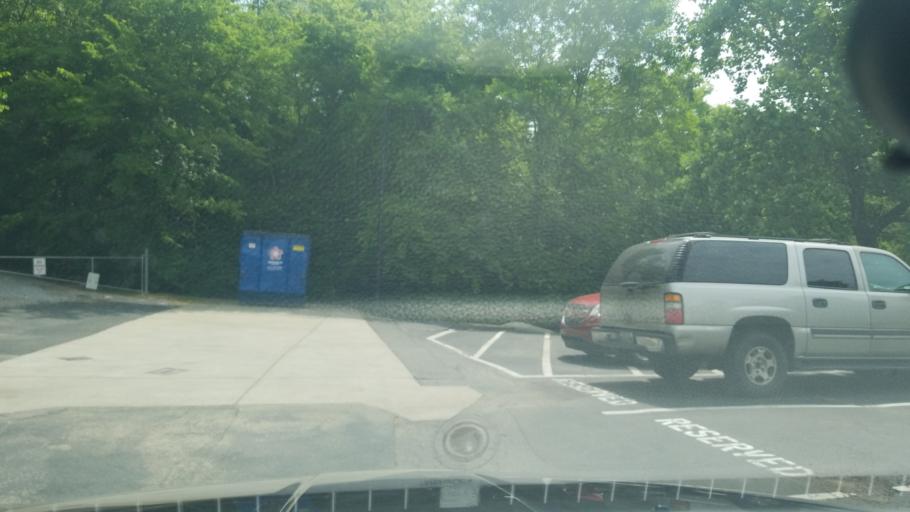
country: US
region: Tennessee
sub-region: Davidson County
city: Goodlettsville
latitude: 36.2681
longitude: -86.7399
